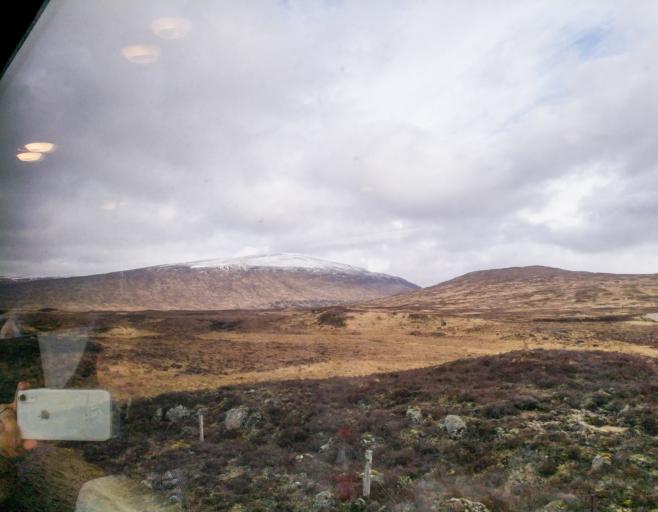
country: GB
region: Scotland
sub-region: Highland
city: Spean Bridge
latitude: 56.7445
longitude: -4.6697
